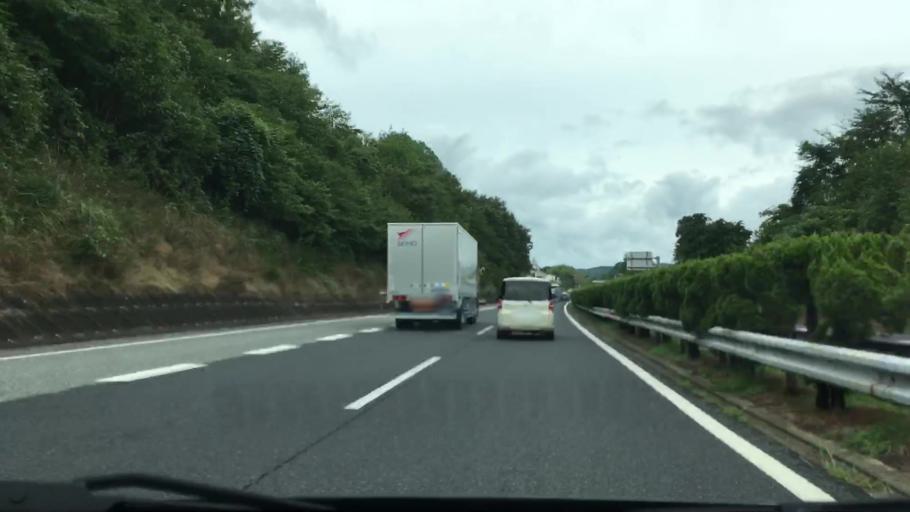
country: JP
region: Okayama
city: Tsuyama
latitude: 35.0275
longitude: 134.1594
